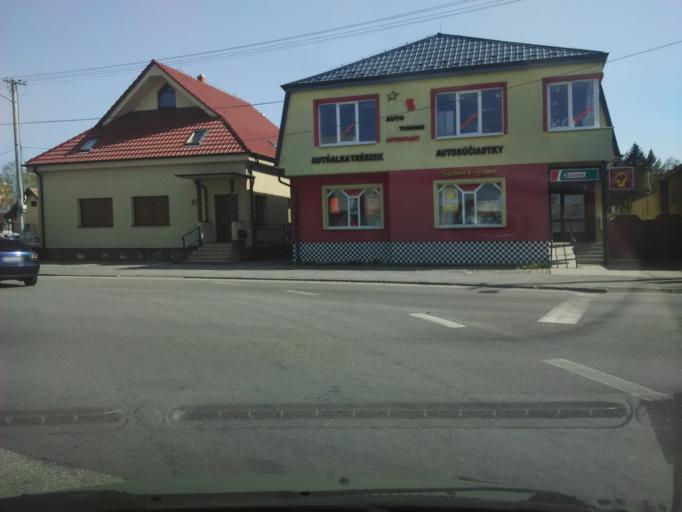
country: SK
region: Nitriansky
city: Sellye
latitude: 48.1522
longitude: 17.8693
